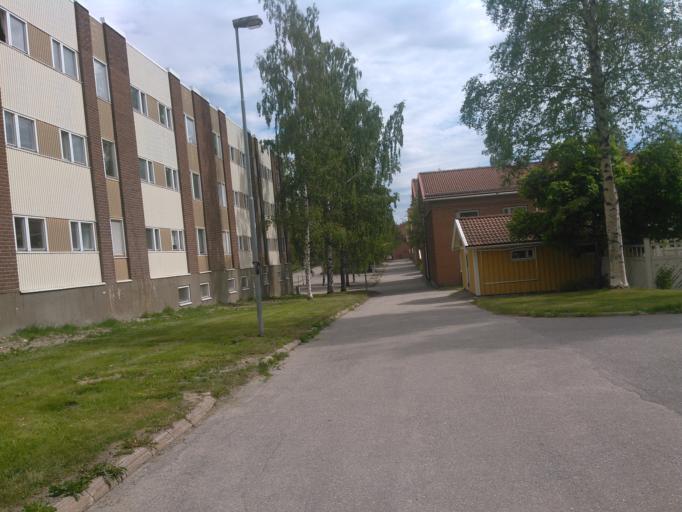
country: SE
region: Vaesterbotten
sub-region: Umea Kommun
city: Umea
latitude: 63.8093
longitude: 20.3081
